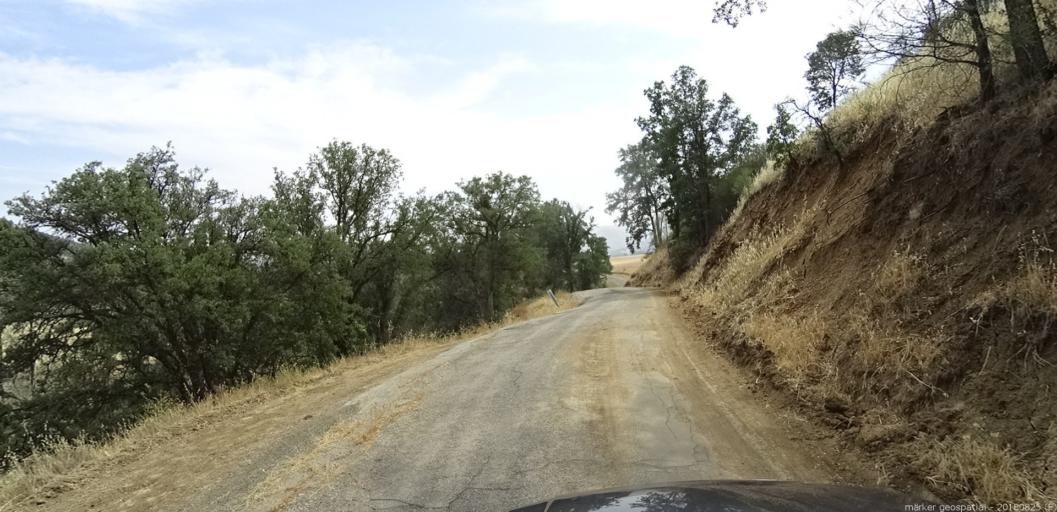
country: US
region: California
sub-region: Fresno County
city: Coalinga
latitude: 36.2206
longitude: -120.7072
